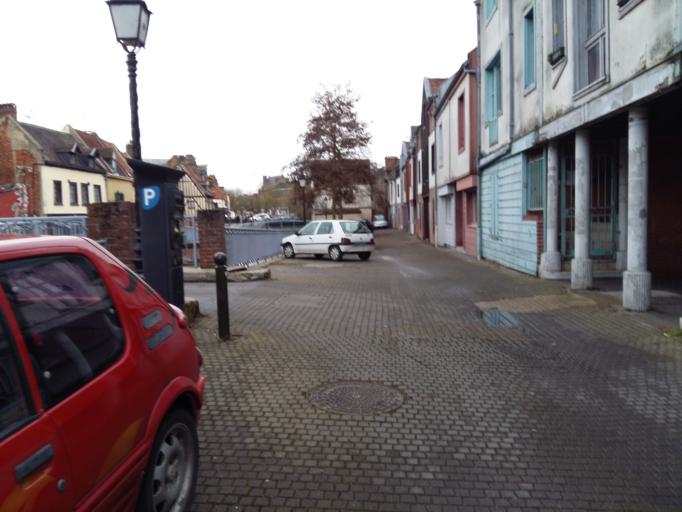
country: FR
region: Picardie
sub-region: Departement de la Somme
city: Amiens
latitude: 49.8973
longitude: 2.3031
